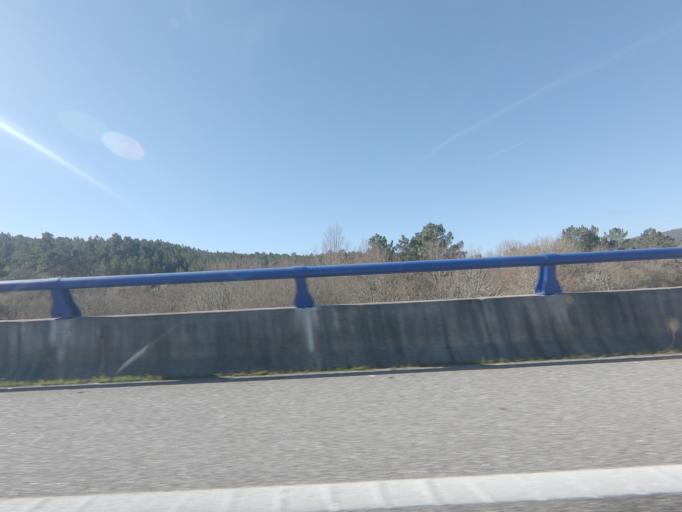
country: ES
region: Galicia
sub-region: Provincia de Ourense
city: Cea
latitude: 42.4621
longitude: -8.0257
